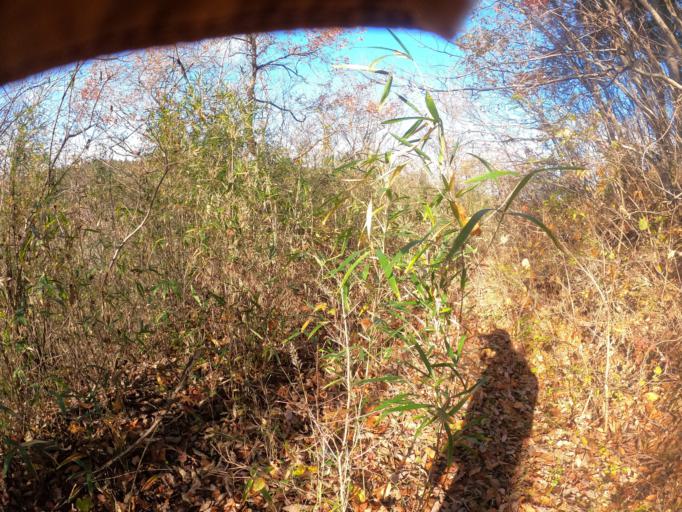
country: JP
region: Iwate
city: Ichinoseki
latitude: 38.8864
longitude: 141.1285
